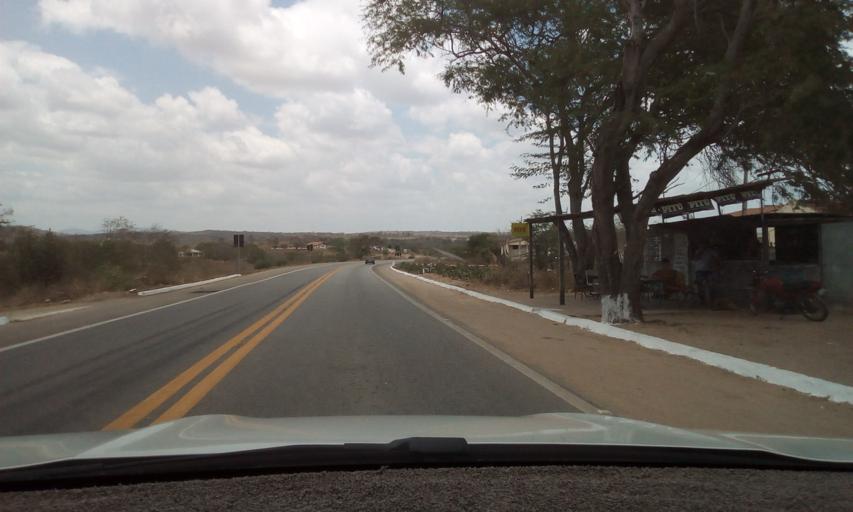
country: BR
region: Pernambuco
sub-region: Taquaritinga Do Norte
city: Taquaritinga do Norte
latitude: -7.7039
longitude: -36.0627
